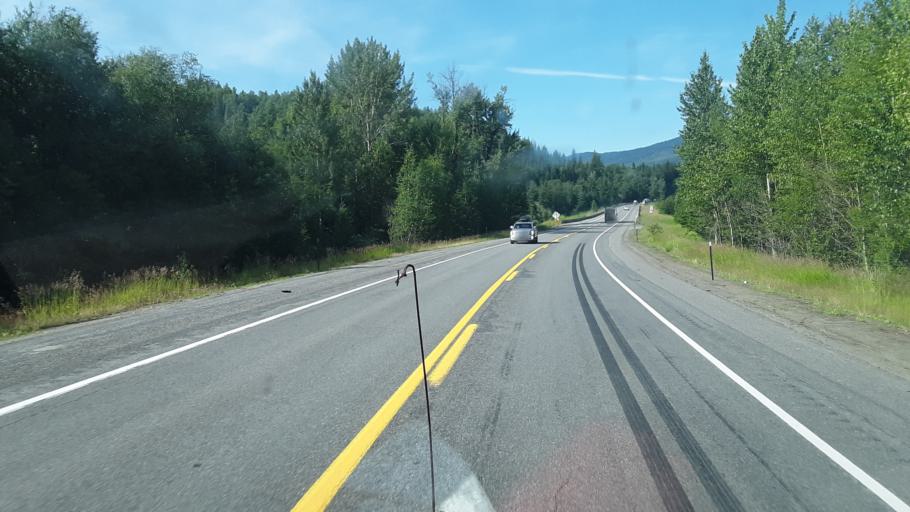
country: US
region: Idaho
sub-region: Bonner County
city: Ponderay
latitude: 48.4234
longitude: -116.4972
